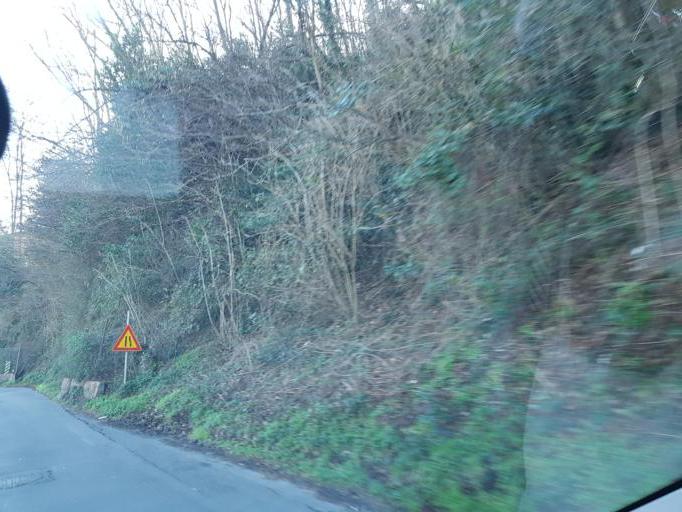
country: IT
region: Liguria
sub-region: Provincia di Genova
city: Santa Marta
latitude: 44.5053
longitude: 8.8912
